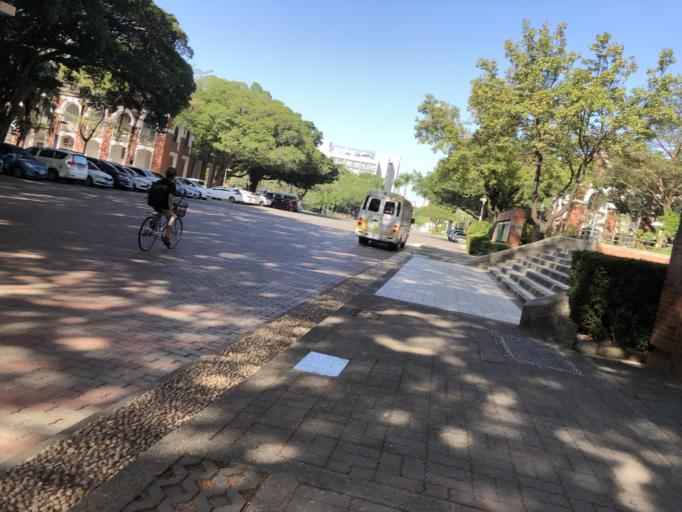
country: TW
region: Taiwan
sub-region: Tainan
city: Tainan
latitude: 22.9990
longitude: 120.2167
